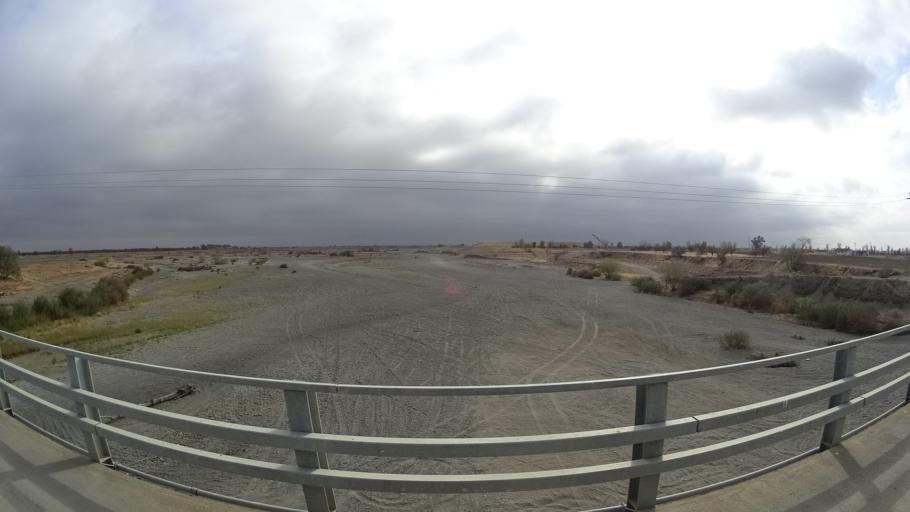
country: US
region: California
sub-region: Yolo County
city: Esparto
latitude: 38.7128
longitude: -122.0112
